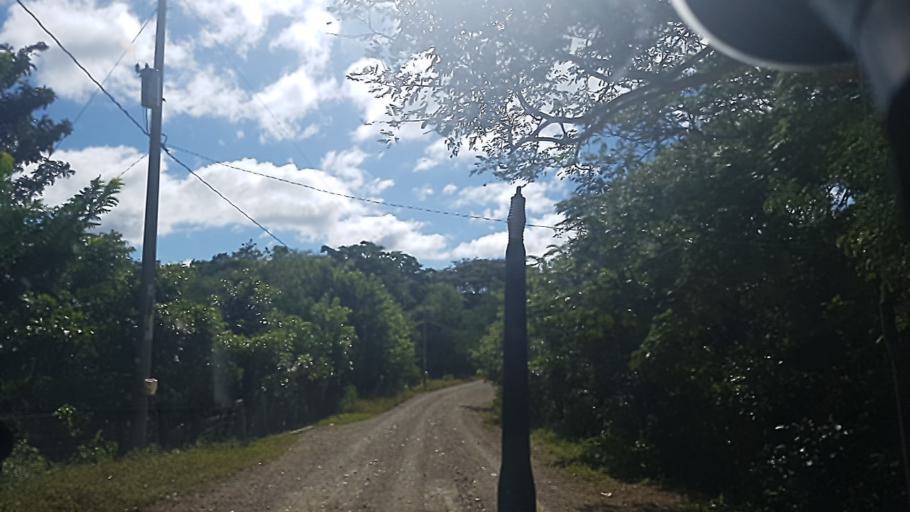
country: NI
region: Carazo
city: Santa Teresa
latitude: 11.6325
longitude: -86.1681
